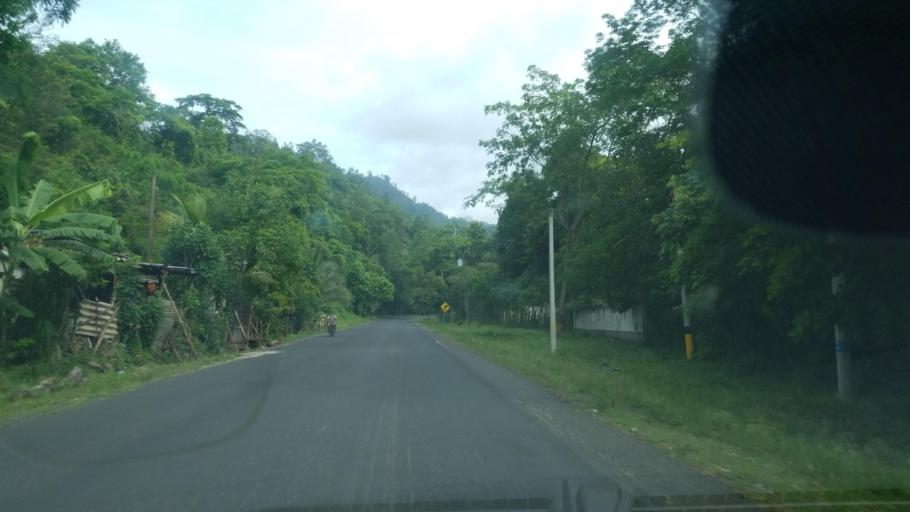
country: HN
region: Santa Barbara
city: Petoa
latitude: 15.2414
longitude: -88.2681
